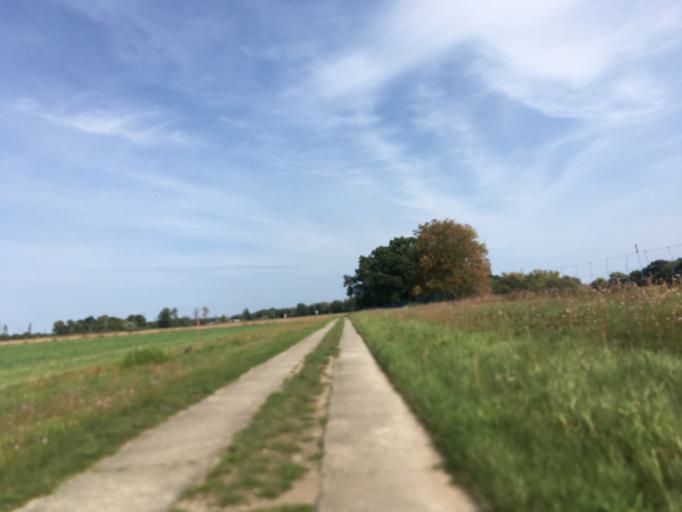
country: DE
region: Brandenburg
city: Guben
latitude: 52.0049
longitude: 14.7139
